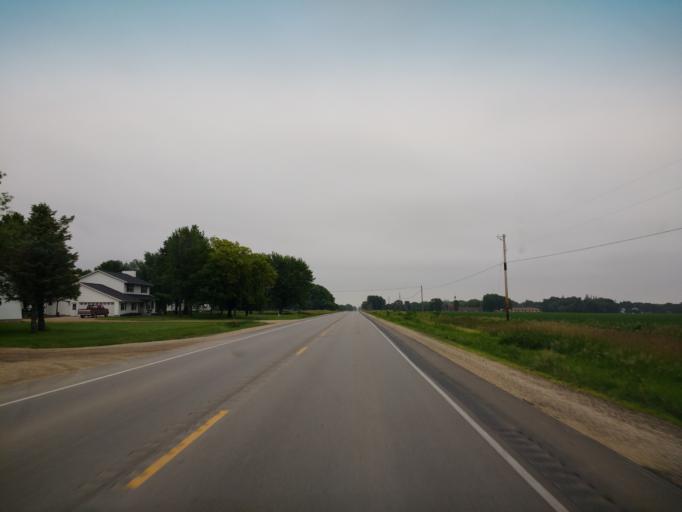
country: US
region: Iowa
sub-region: O'Brien County
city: Hartley
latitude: 43.1849
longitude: -95.4976
